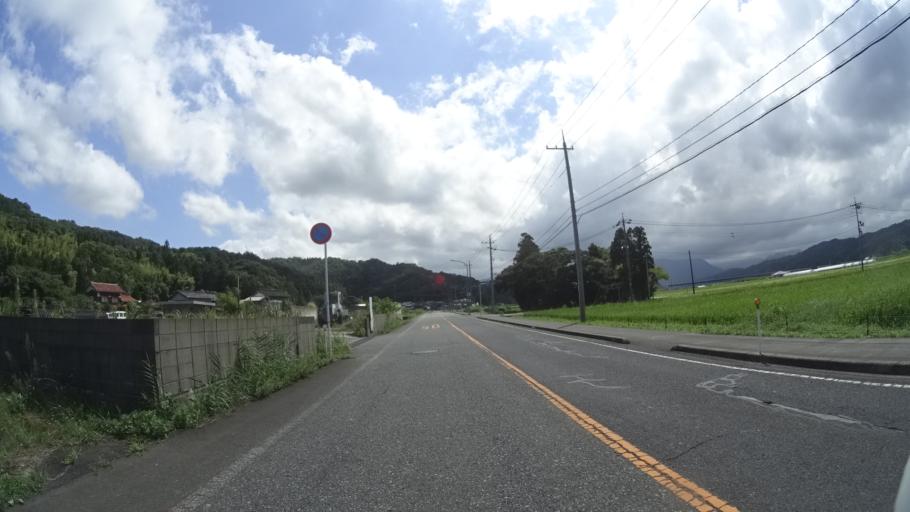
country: JP
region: Tottori
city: Tottori
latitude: 35.5082
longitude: 134.0811
